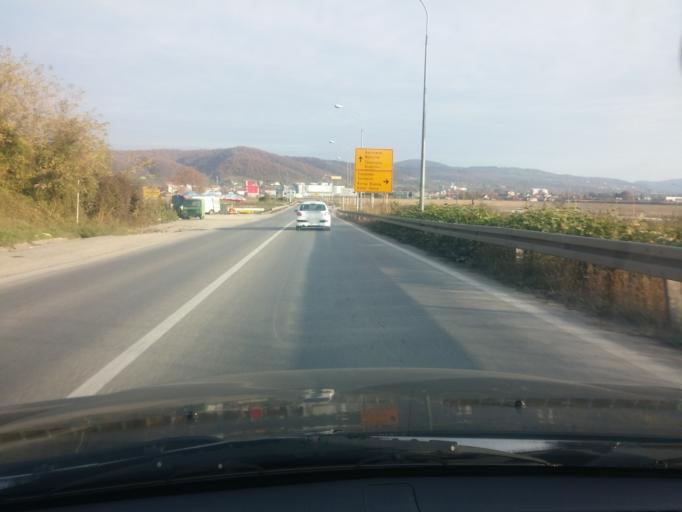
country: BA
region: Republika Srpska
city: Banja Luka
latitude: 44.8202
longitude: 17.1997
